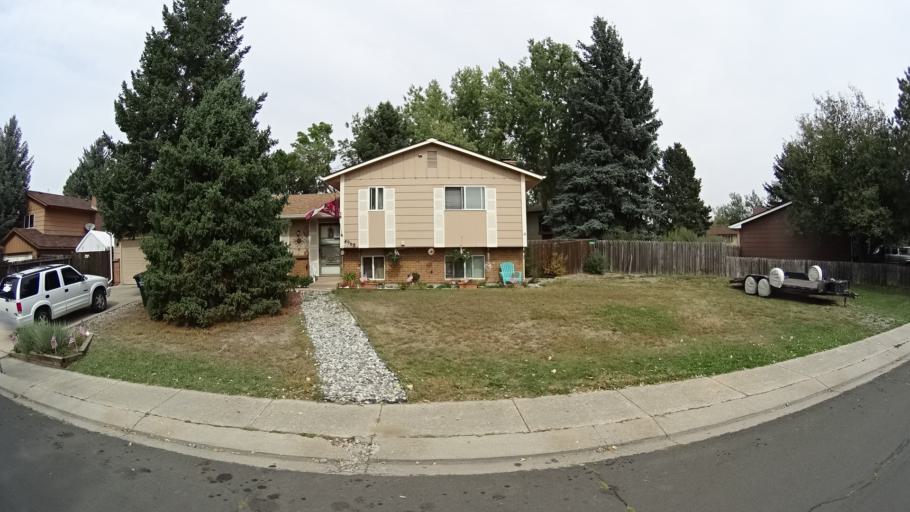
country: US
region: Colorado
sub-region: El Paso County
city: Cimarron Hills
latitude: 38.9008
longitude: -104.7398
